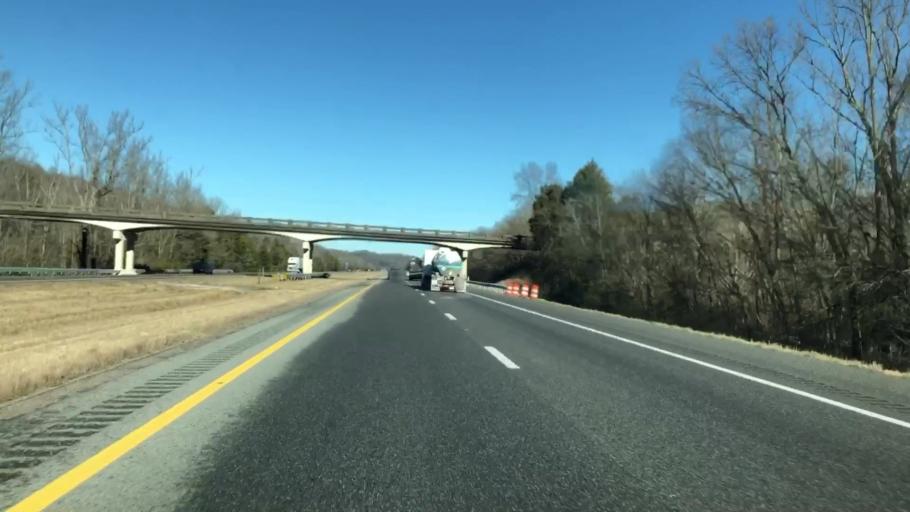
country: US
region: Alabama
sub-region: Limestone County
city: Ardmore
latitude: 35.1374
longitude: -86.8779
